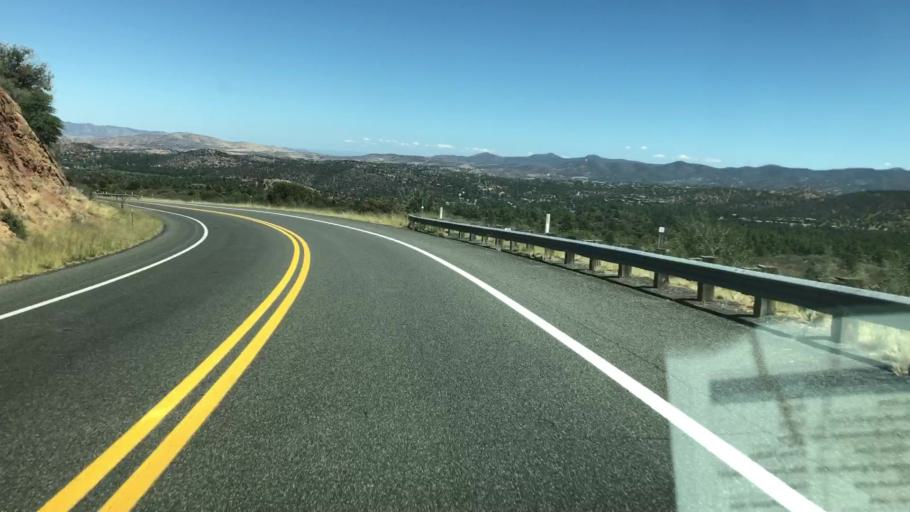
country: US
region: Arizona
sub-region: Yavapai County
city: Prescott
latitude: 34.5818
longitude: -112.5464
